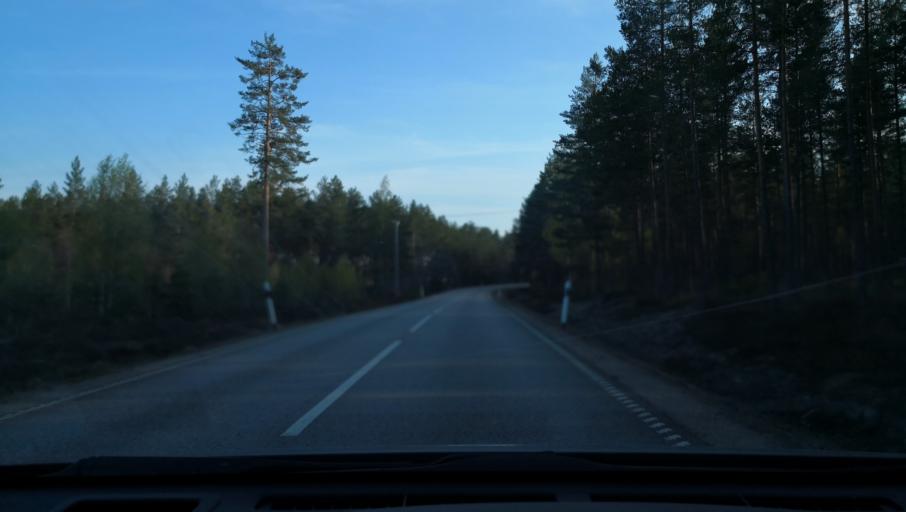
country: SE
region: Uppsala
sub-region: Heby Kommun
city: Heby
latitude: 60.0273
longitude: 16.8521
